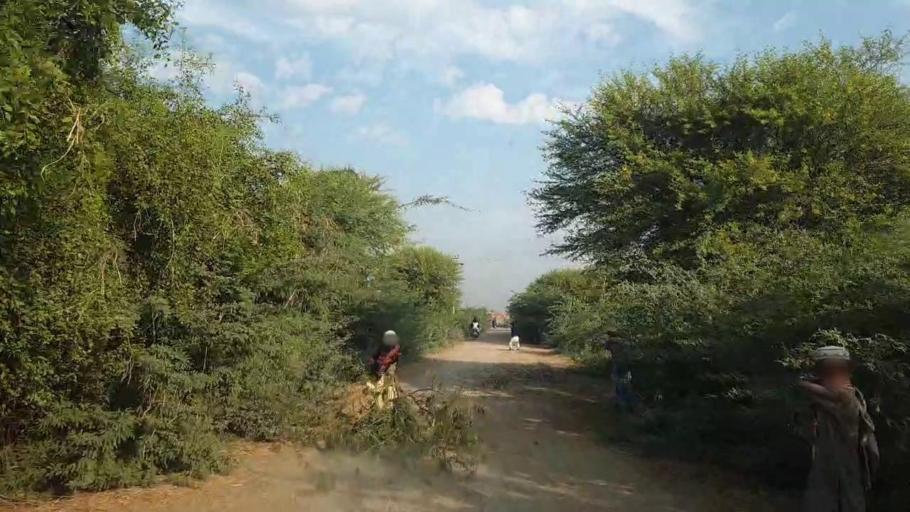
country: PK
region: Sindh
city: Tando Bago
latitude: 24.8065
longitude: 68.9585
